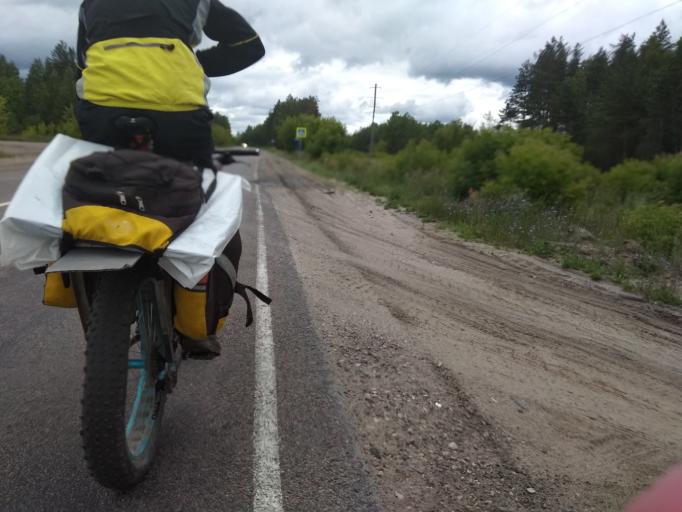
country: RU
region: Moskovskaya
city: Kerva
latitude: 55.5789
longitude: 39.6884
